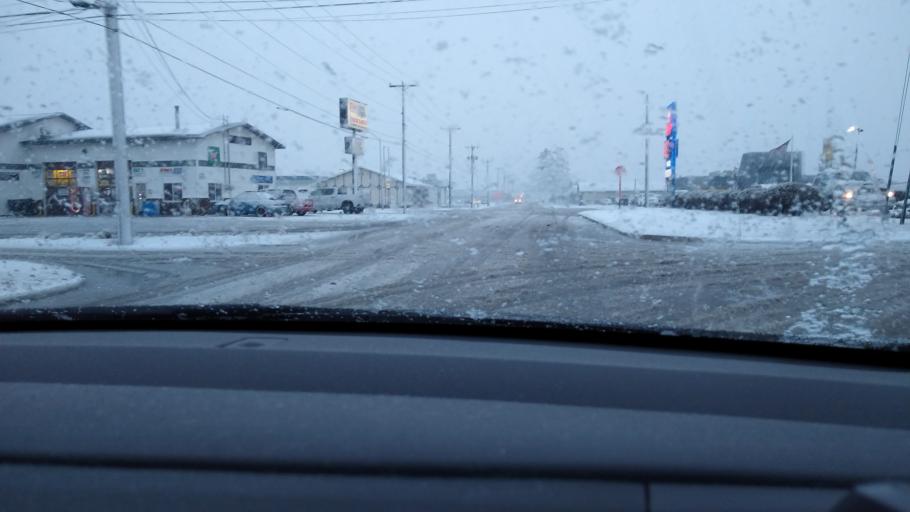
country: US
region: Michigan
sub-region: Delta County
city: Escanaba
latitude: 45.7536
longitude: -87.0762
